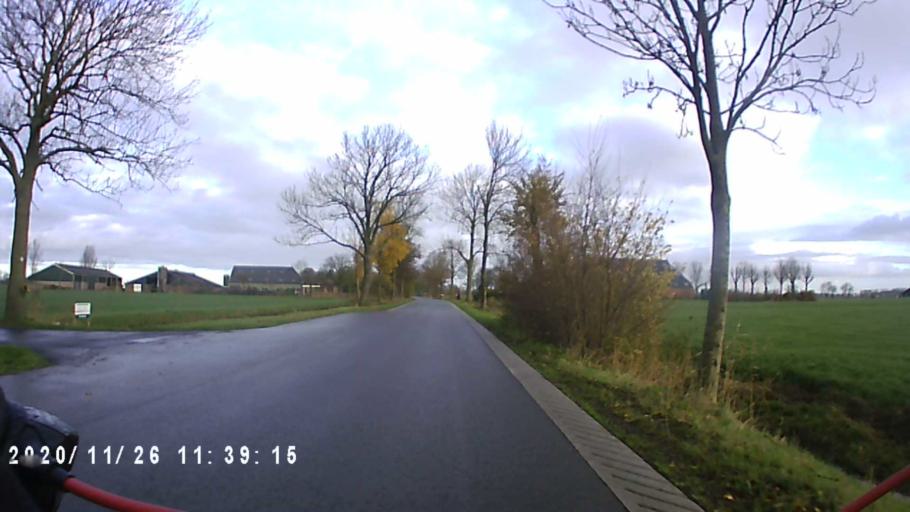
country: NL
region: Groningen
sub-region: Gemeente Bedum
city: Bedum
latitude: 53.2835
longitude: 6.5689
